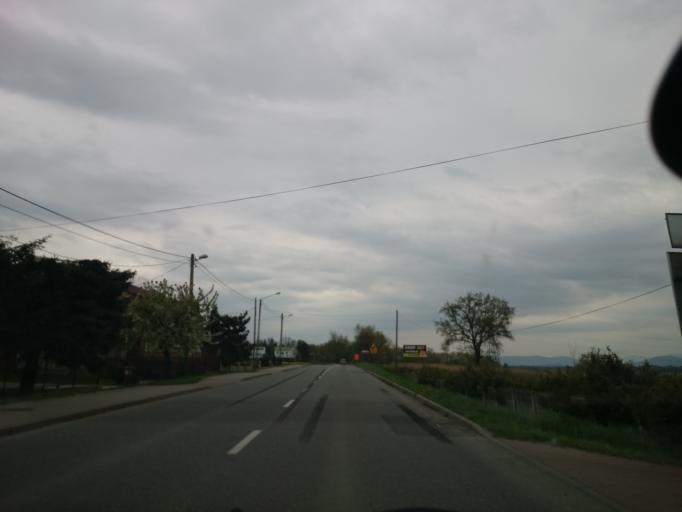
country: PL
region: Opole Voivodeship
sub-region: Powiat nyski
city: Nysa
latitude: 50.4311
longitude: 17.3411
